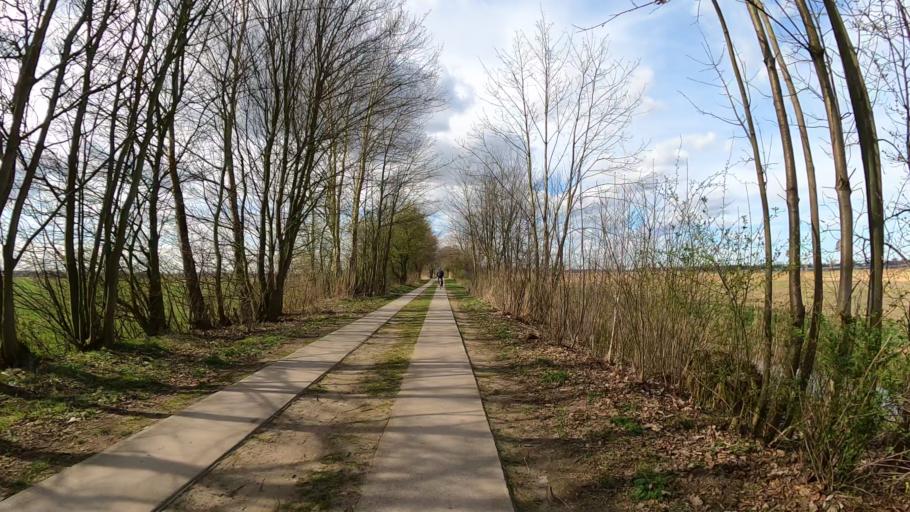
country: DE
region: Lower Saxony
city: Stelle
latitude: 53.4662
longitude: 10.0970
